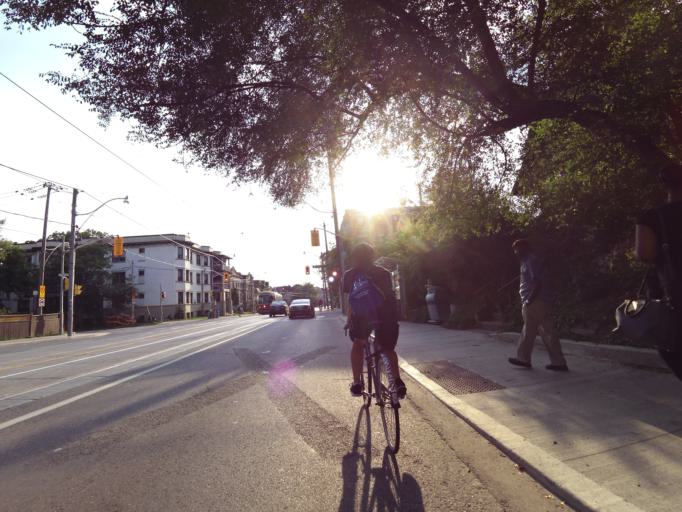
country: CA
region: Ontario
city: Toronto
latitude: 43.6368
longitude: -79.4382
